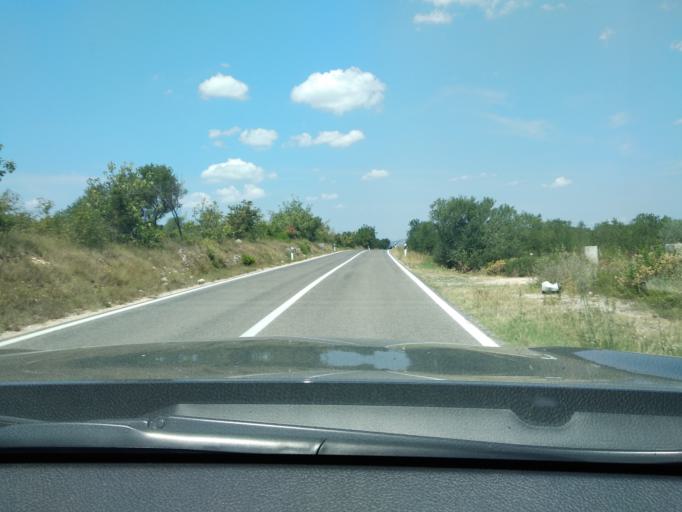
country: HR
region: Sibensko-Kniniska
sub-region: Grad Sibenik
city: Pirovac
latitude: 43.7999
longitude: 15.6750
